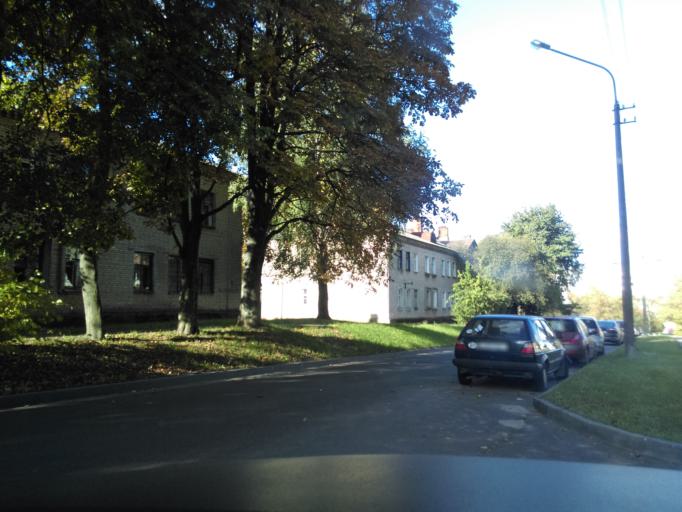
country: BY
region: Minsk
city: Minsk
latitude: 53.9111
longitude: 27.6319
